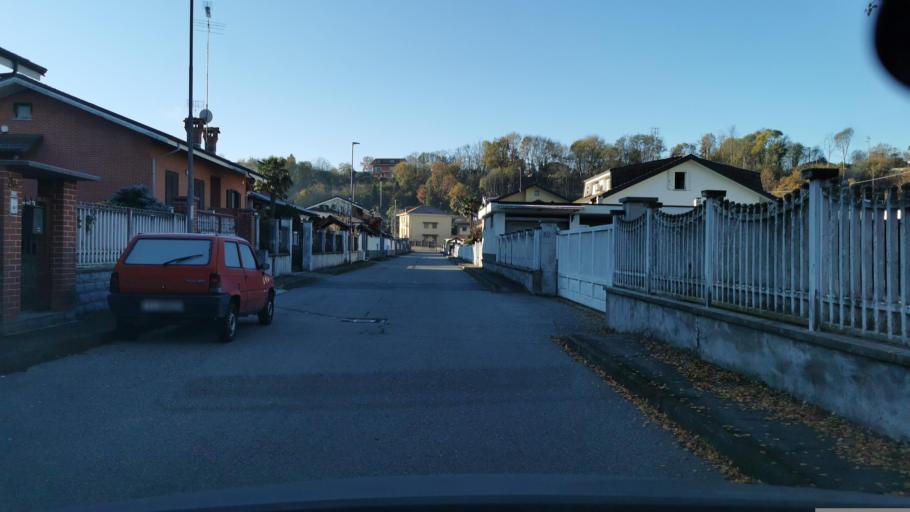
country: IT
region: Piedmont
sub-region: Provincia di Torino
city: Volpiano
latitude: 45.2067
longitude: 7.7727
